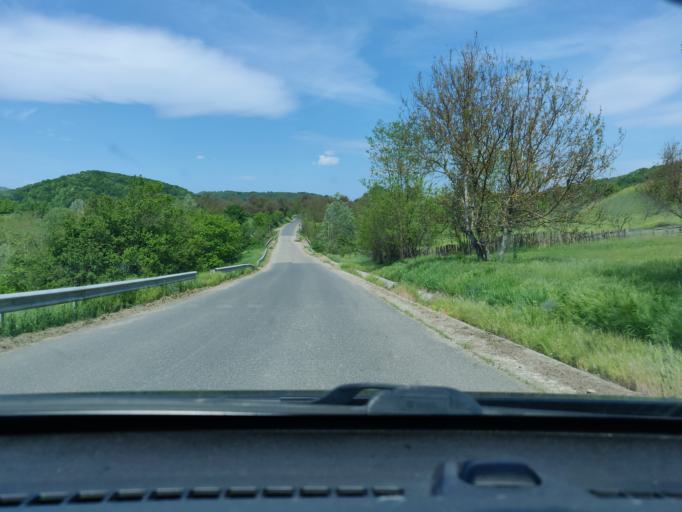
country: RO
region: Vrancea
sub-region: Comuna Vidra
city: Vidra
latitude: 45.9458
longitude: 26.8722
